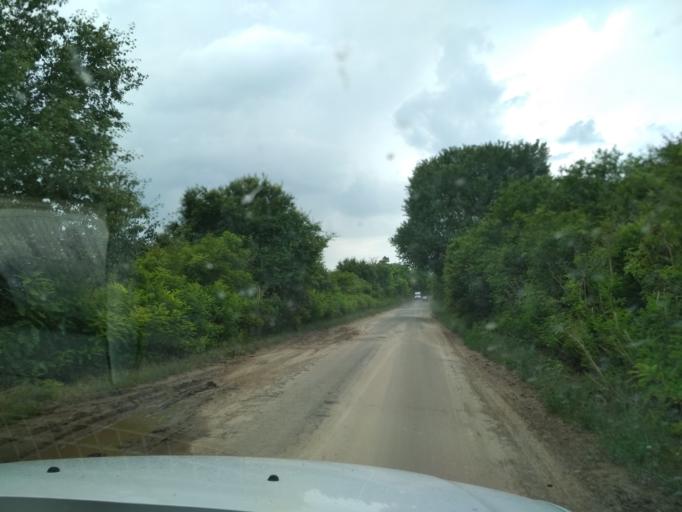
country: HU
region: Pest
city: Albertirsa
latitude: 47.2567
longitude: 19.6503
